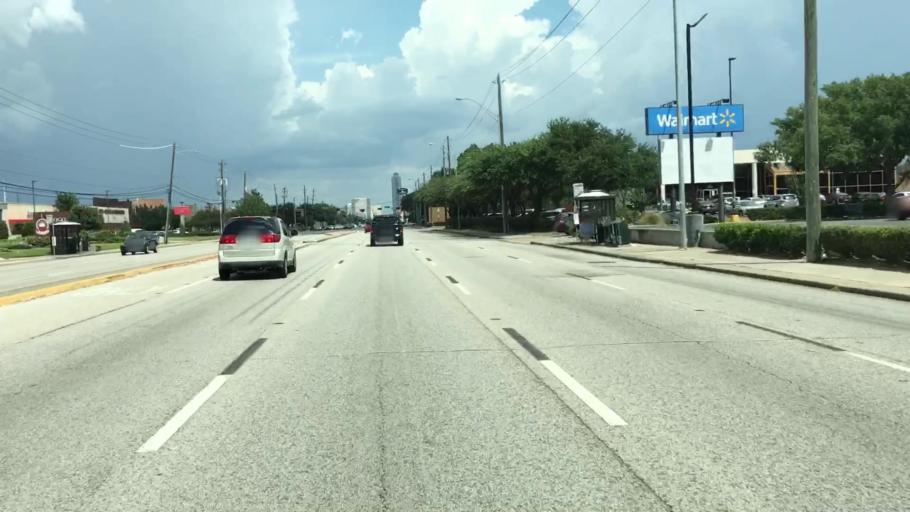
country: US
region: Texas
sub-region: Harris County
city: Piney Point Village
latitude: 29.7375
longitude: -95.5141
